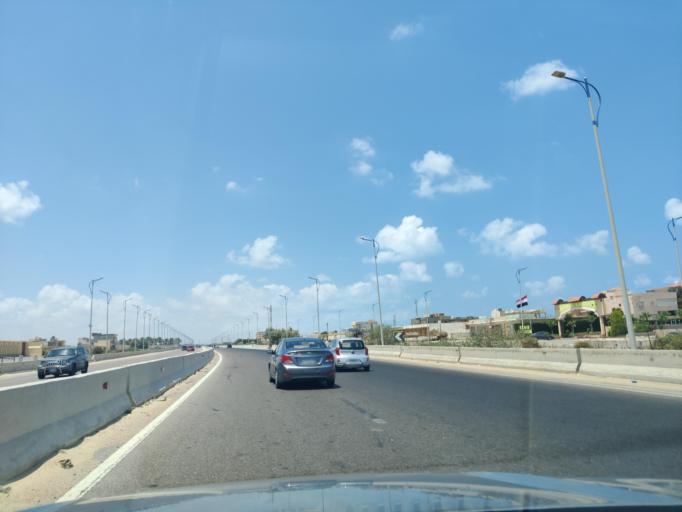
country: EG
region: Alexandria
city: Alexandria
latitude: 30.9857
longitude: 29.5858
